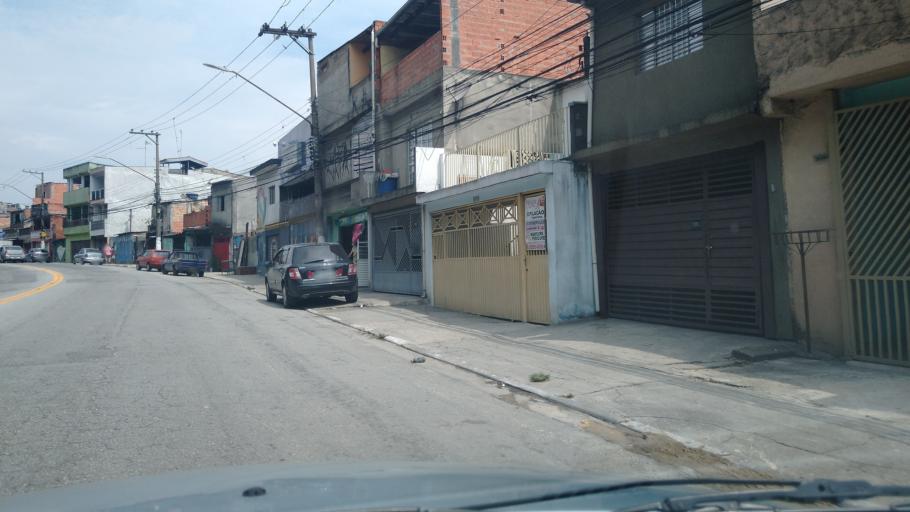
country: BR
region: Sao Paulo
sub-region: Osasco
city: Osasco
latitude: -23.5030
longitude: -46.7787
